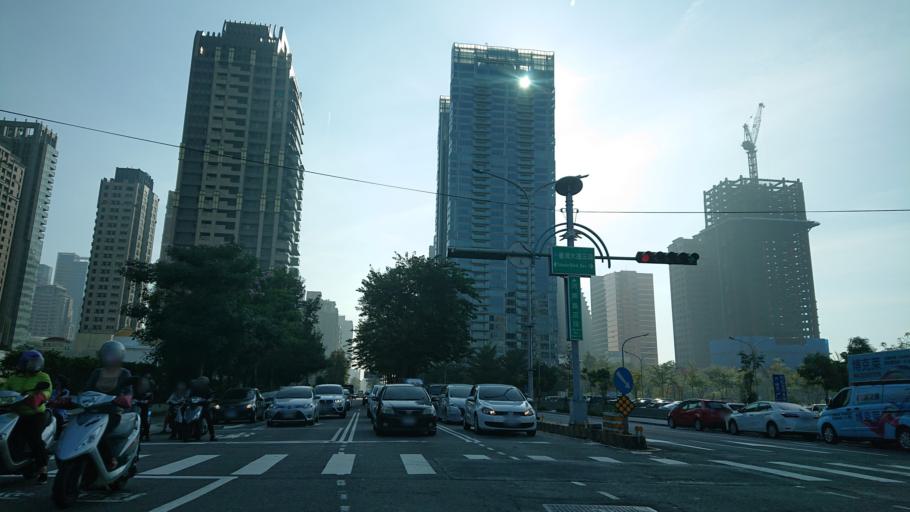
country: TW
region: Taiwan
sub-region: Taichung City
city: Taichung
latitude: 24.1676
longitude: 120.6409
